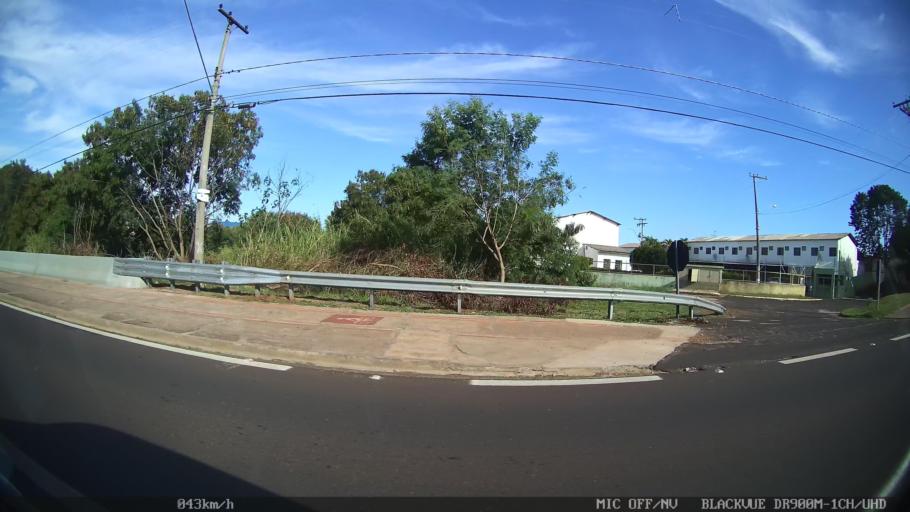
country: BR
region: Sao Paulo
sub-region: Araraquara
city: Araraquara
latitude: -21.7907
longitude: -48.1463
